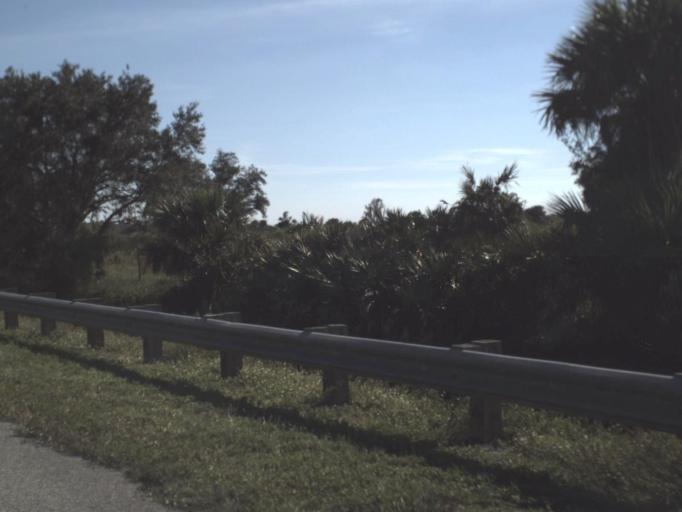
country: US
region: Florida
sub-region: Glades County
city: Moore Haven
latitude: 26.8763
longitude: -81.2242
